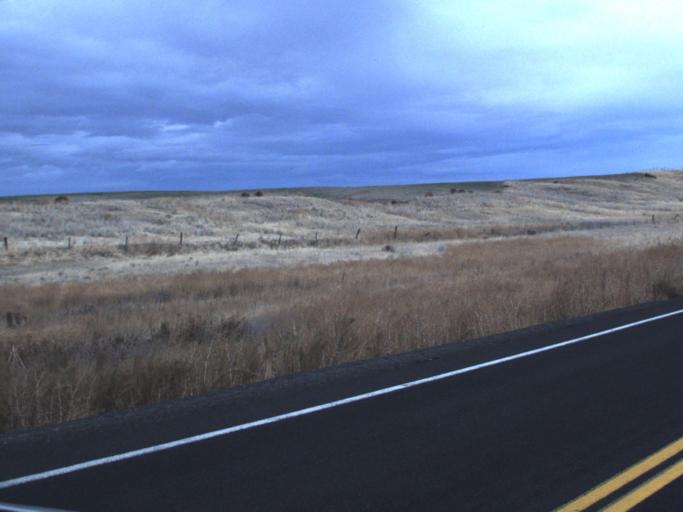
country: US
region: Washington
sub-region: Adams County
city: Ritzville
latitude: 47.3936
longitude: -118.6896
